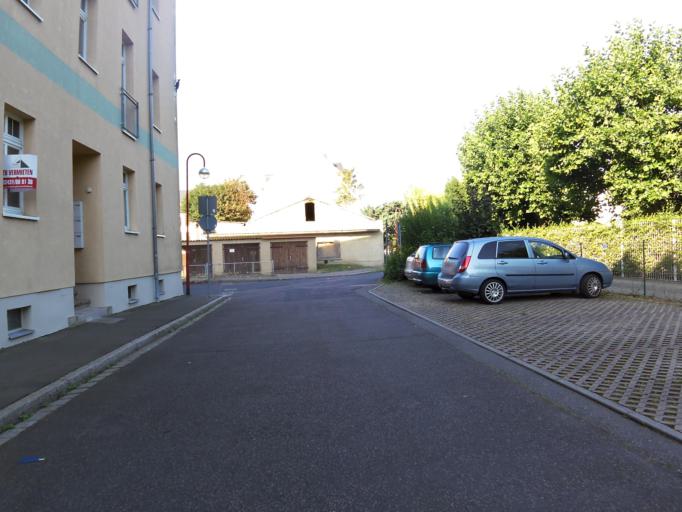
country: DE
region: Saxony
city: Dobeln
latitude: 51.1204
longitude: 13.1269
